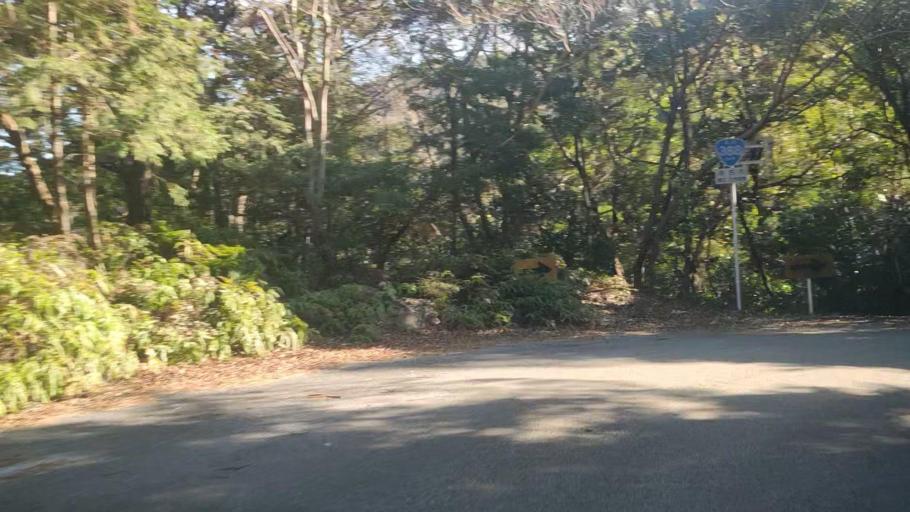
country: JP
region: Oita
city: Saiki
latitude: 32.7851
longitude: 131.8618
